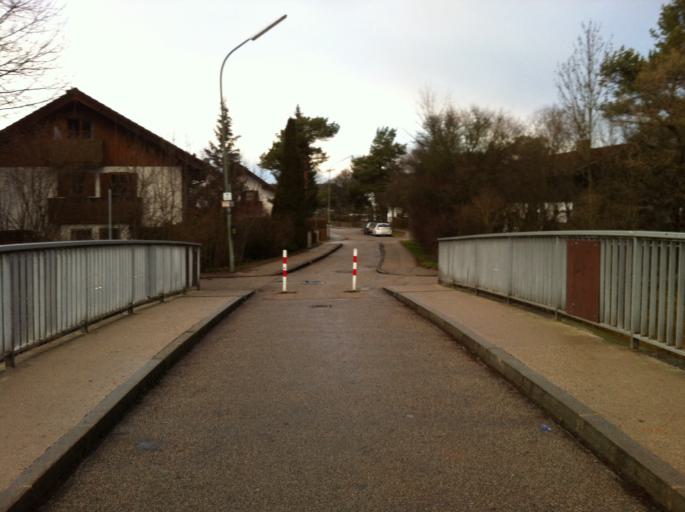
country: DE
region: Bavaria
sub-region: Upper Bavaria
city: Wolfratshausen
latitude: 47.9038
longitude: 11.4402
